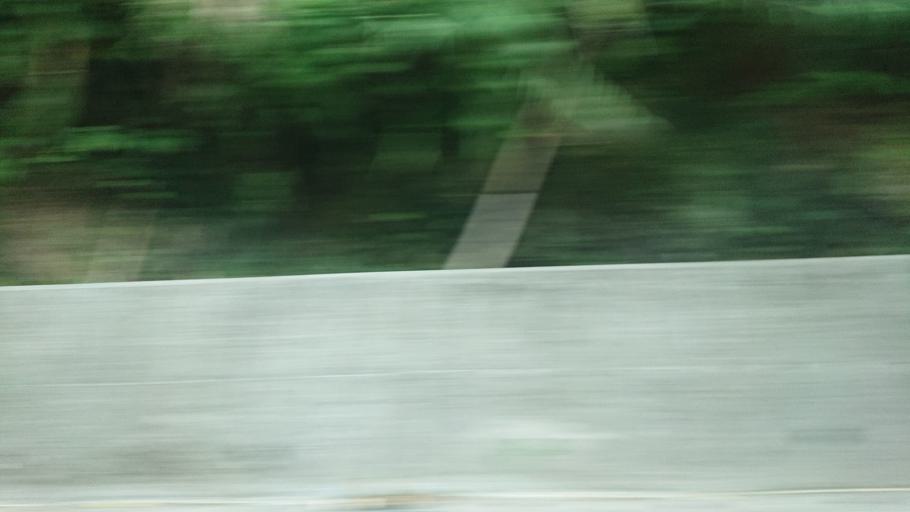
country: TW
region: Taiwan
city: Daxi
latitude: 24.8754
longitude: 121.3834
